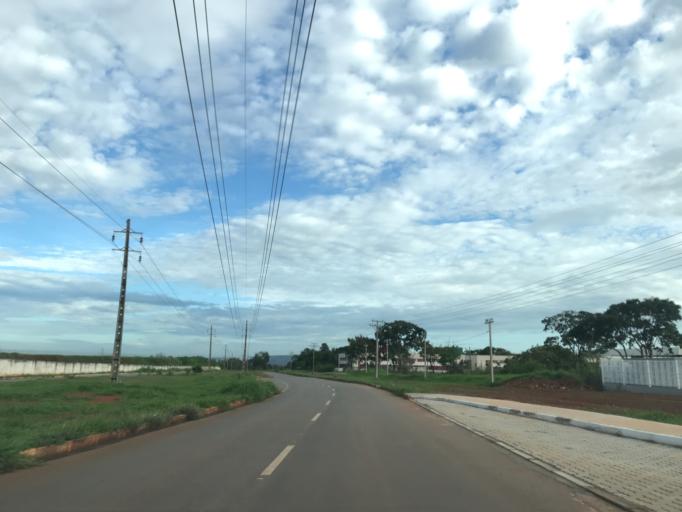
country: BR
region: Federal District
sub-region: Brasilia
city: Brasilia
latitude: -15.7746
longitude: -47.8951
